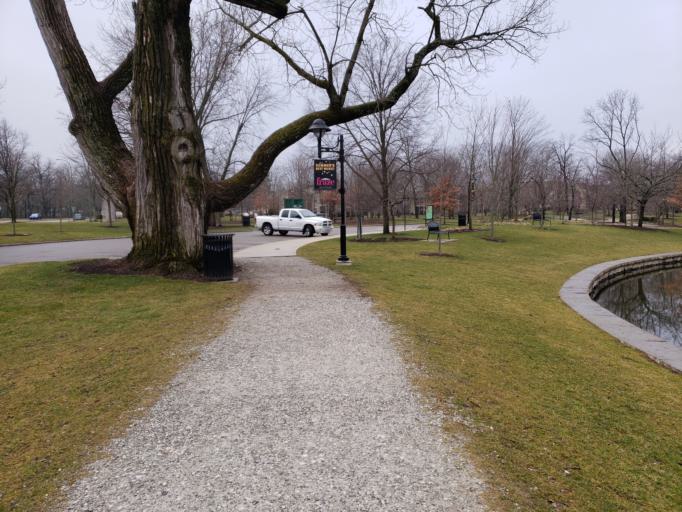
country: US
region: Ohio
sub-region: Montgomery County
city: Kettering
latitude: 39.6973
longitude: -84.1539
